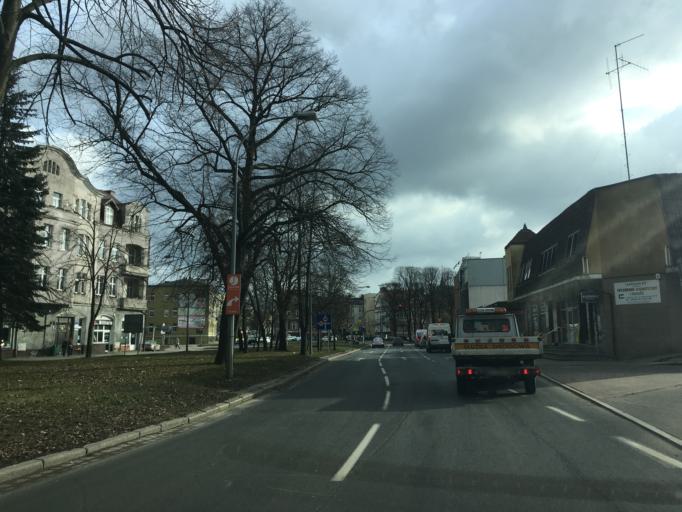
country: PL
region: Pomeranian Voivodeship
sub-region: Slupsk
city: Slupsk
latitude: 54.4701
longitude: 17.0280
